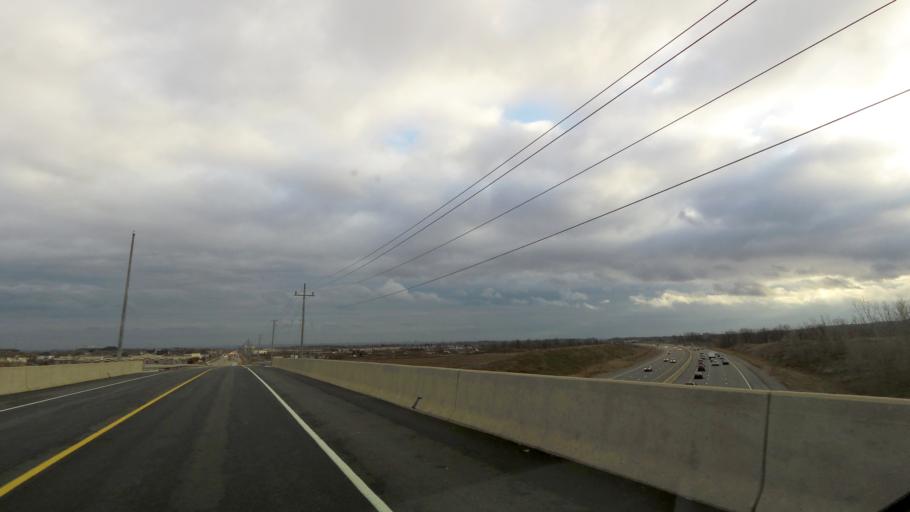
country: CA
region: Ontario
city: Burlington
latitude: 43.3990
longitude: -79.8332
